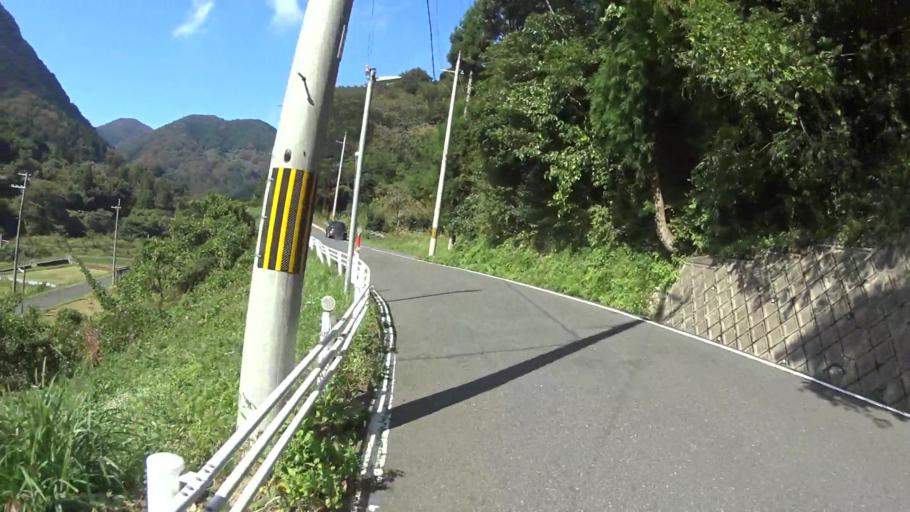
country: JP
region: Kyoto
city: Miyazu
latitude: 35.7411
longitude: 135.2454
